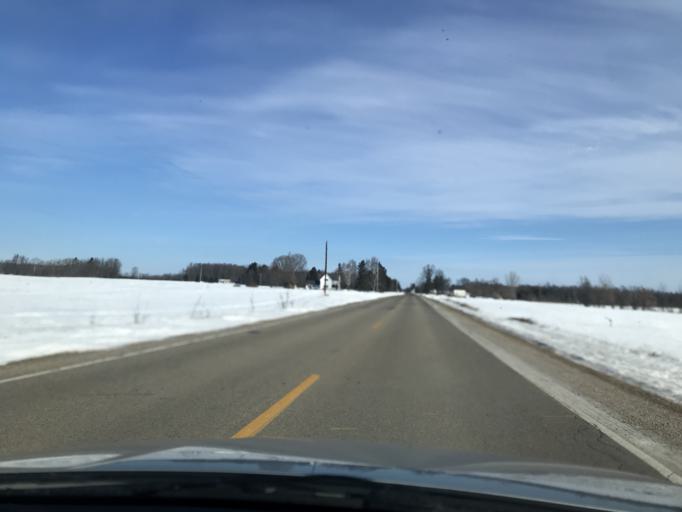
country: US
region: Wisconsin
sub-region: Oconto County
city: Oconto Falls
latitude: 44.9028
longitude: -88.1555
